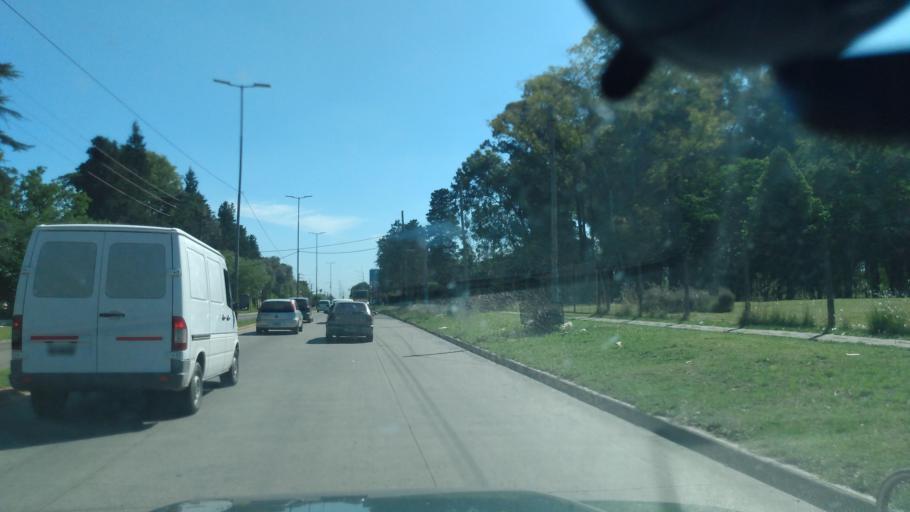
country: AR
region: Buenos Aires
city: Hurlingham
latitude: -34.5590
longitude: -58.7304
